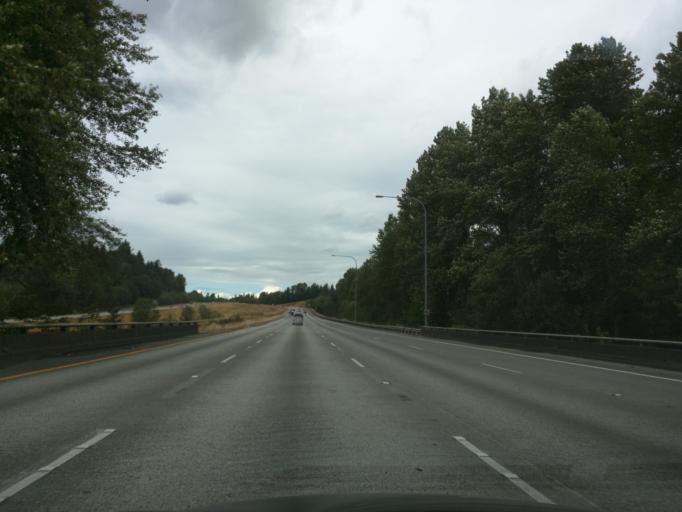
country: US
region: Washington
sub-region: Snohomish County
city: Bryant
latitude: 48.2145
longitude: -122.2175
